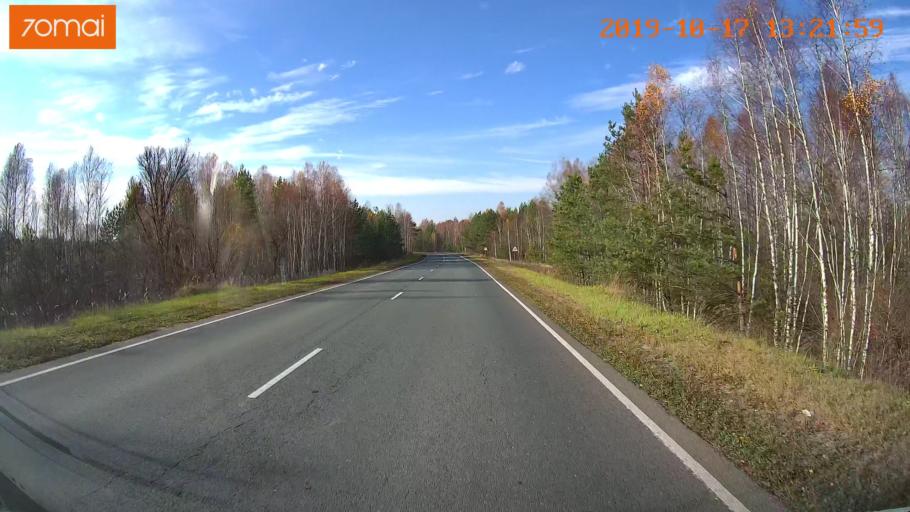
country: RU
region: Rjazan
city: Gus'-Zheleznyy
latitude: 55.0840
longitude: 41.0143
